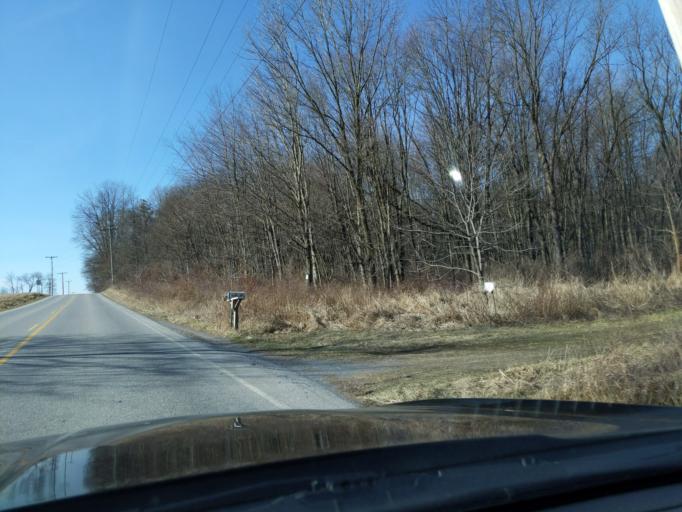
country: US
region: Pennsylvania
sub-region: Blair County
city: Martinsburg
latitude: 40.3658
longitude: -78.2431
